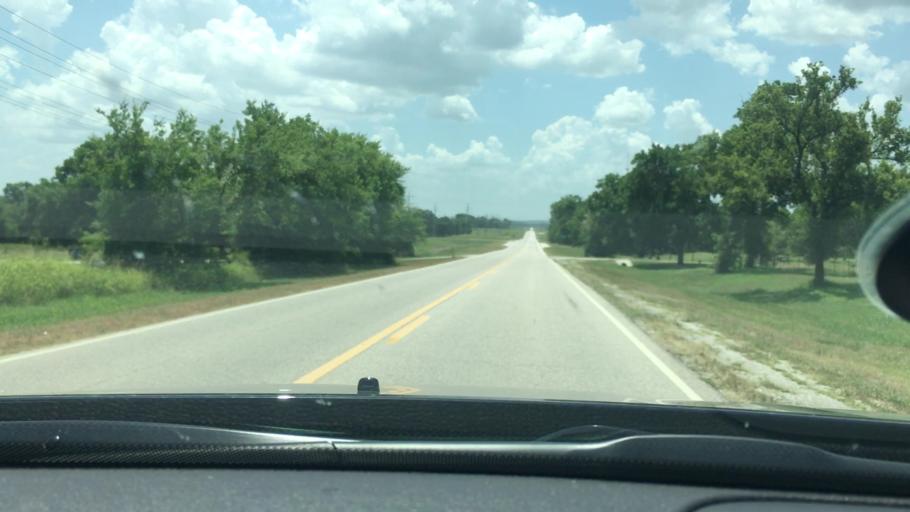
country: US
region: Oklahoma
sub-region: Pontotoc County
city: Ada
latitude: 34.6620
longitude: -96.6349
